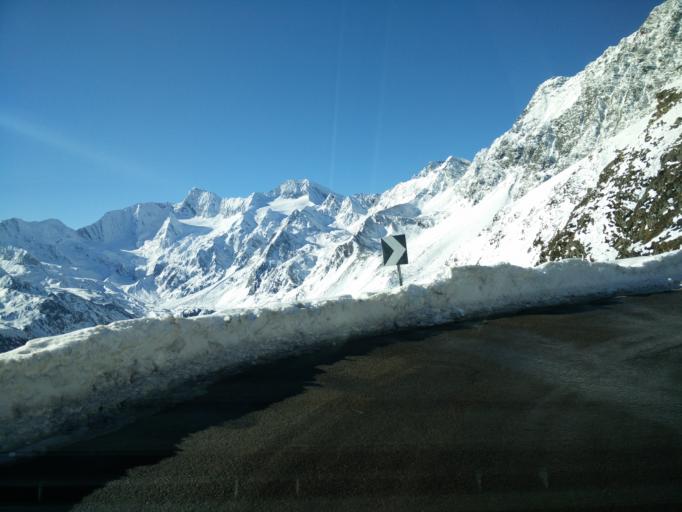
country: IT
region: Trentino-Alto Adige
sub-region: Bolzano
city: Moso in Passiria
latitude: 46.8855
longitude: 11.1111
